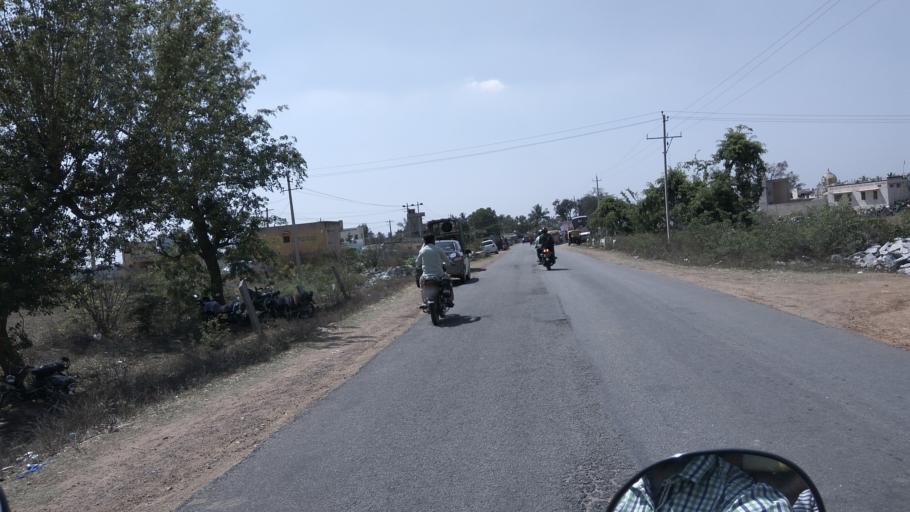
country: IN
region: Karnataka
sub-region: Kolar
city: Mulbagal
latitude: 13.1664
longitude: 78.3664
